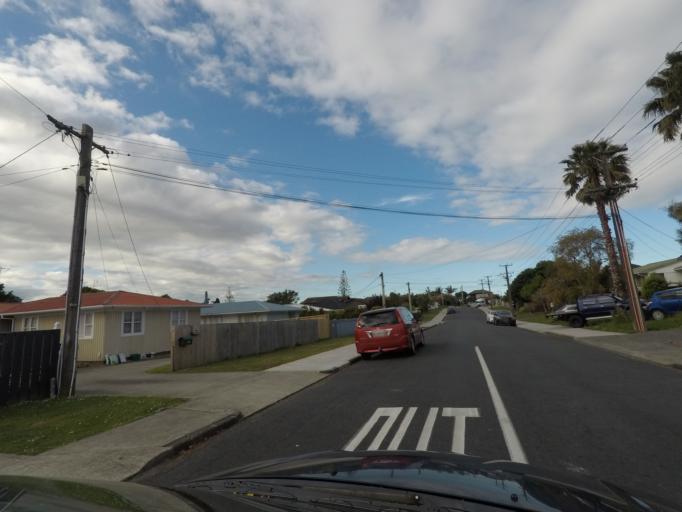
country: NZ
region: Auckland
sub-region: Auckland
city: Rosebank
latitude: -36.8901
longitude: 174.6548
